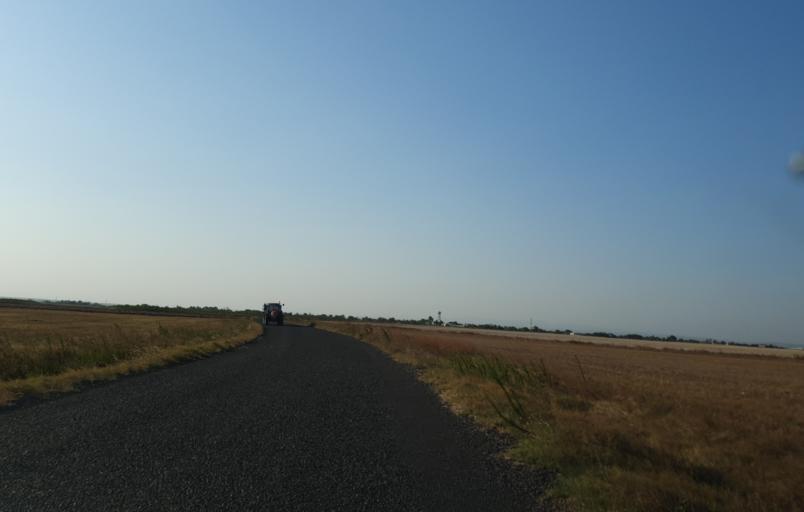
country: TR
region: Tekirdag
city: Beyazkoy
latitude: 41.4229
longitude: 27.7621
